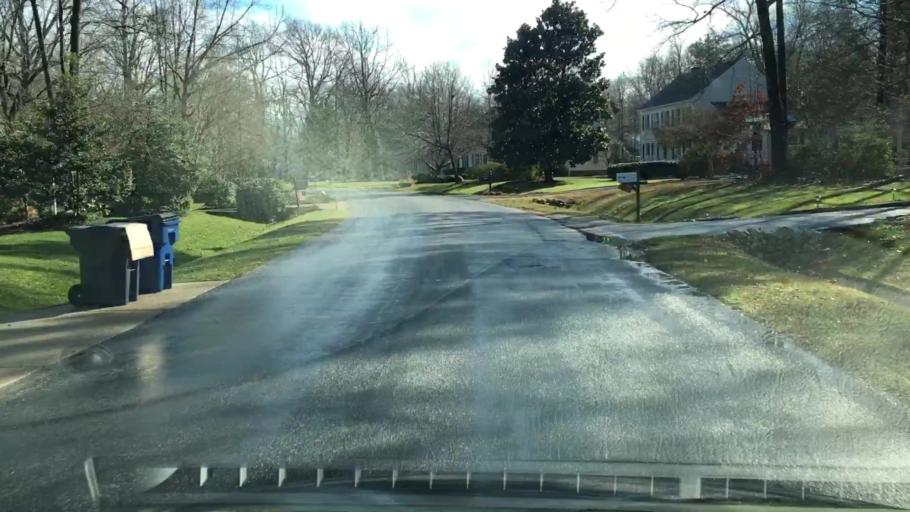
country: US
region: Virginia
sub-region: Chesterfield County
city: Bon Air
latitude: 37.5305
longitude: -77.6043
